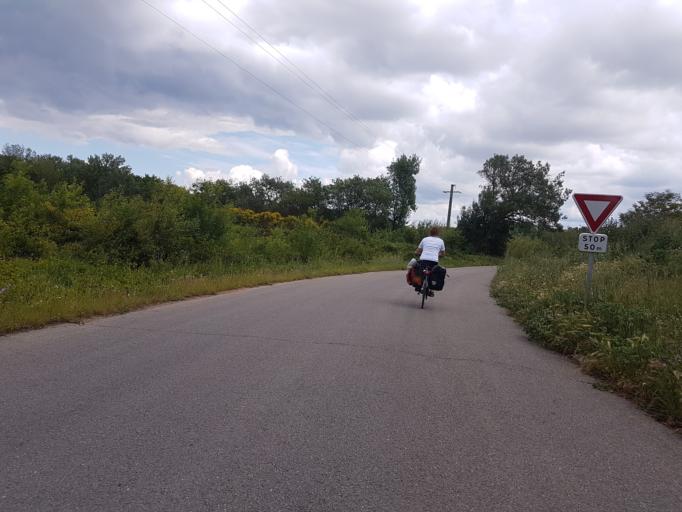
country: FR
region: Languedoc-Roussillon
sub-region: Departement du Gard
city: Beaucaire
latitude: 43.8182
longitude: 4.6379
